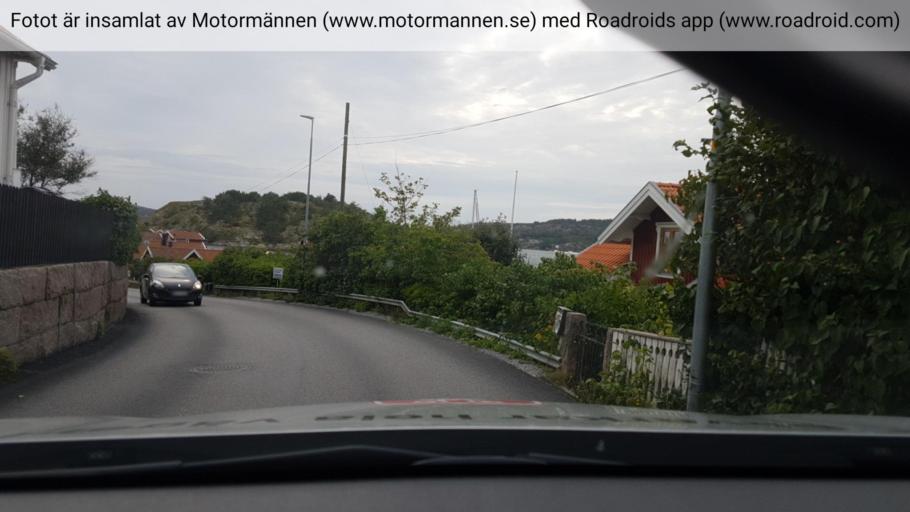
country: SE
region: Vaestra Goetaland
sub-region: Tanums Kommun
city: Grebbestad
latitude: 58.6060
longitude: 11.2809
